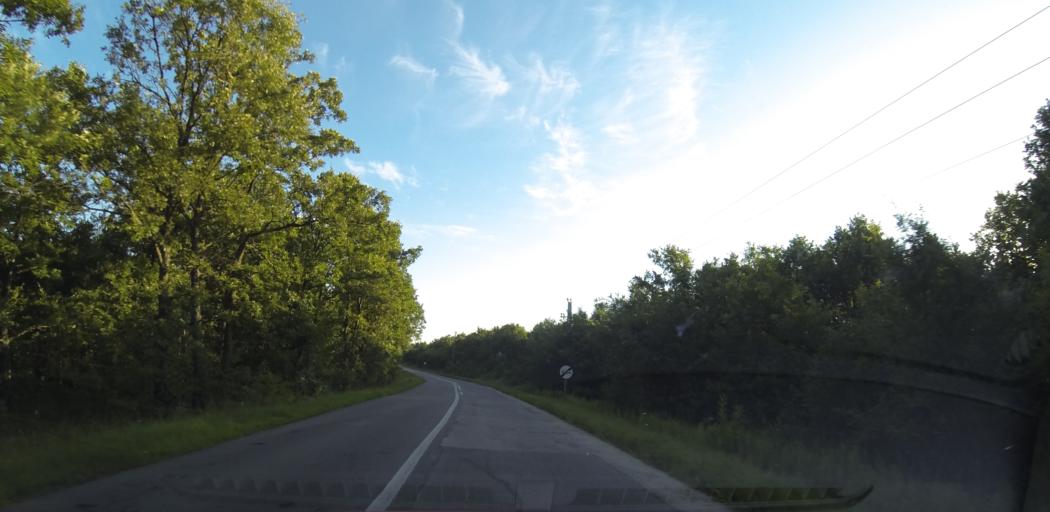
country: RO
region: Dolj
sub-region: Comuna Murgasu
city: Murgasi
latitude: 44.4986
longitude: 23.8932
